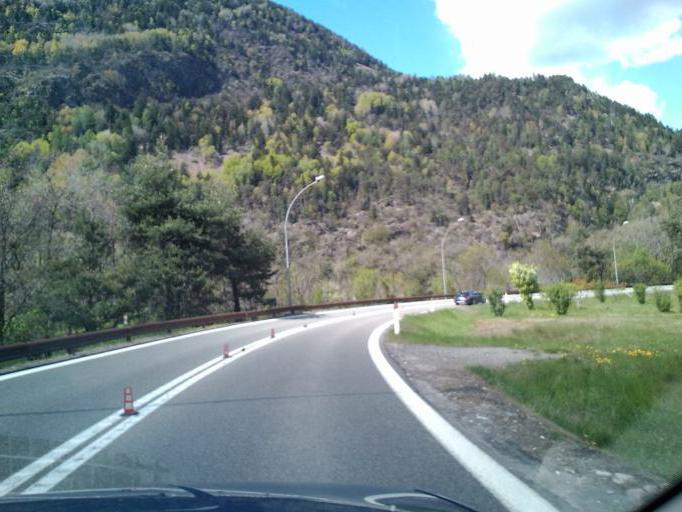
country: IT
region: Trentino-Alto Adige
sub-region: Bolzano
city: Varna
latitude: 46.7639
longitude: 11.6374
